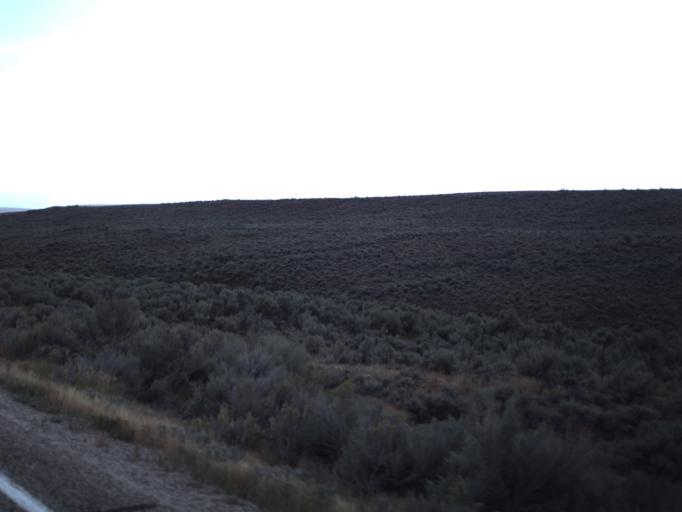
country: US
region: Utah
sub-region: Rich County
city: Randolph
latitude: 41.7921
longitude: -111.2185
